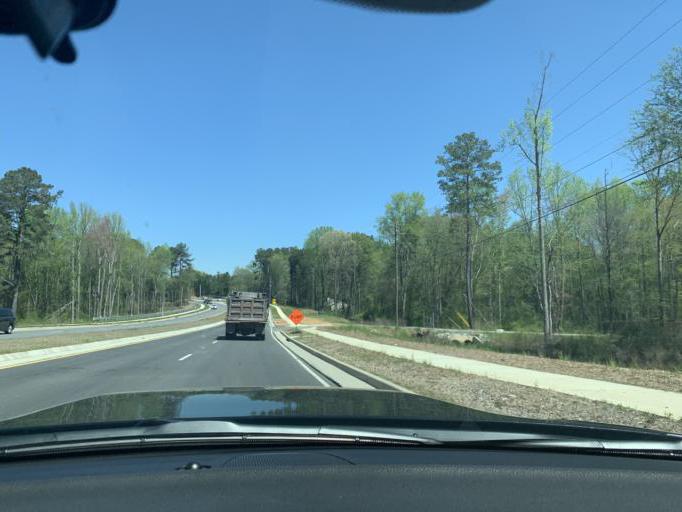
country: US
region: Georgia
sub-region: Forsyth County
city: Cumming
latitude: 34.2096
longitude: -84.1979
